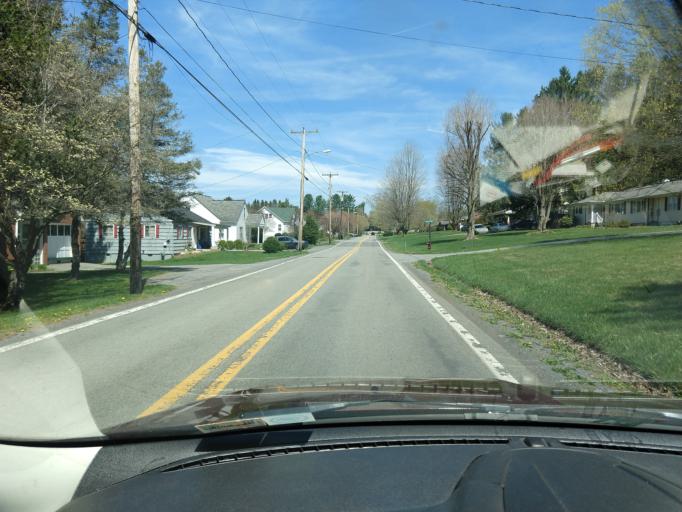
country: US
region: West Virginia
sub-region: Greenbrier County
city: Lewisburg
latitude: 37.7953
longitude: -80.4412
